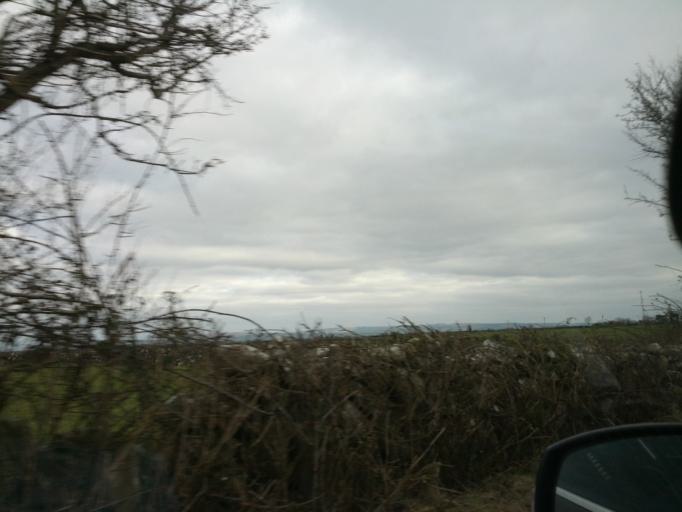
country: IE
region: Connaught
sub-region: County Galway
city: Gort
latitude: 53.1621
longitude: -8.8756
